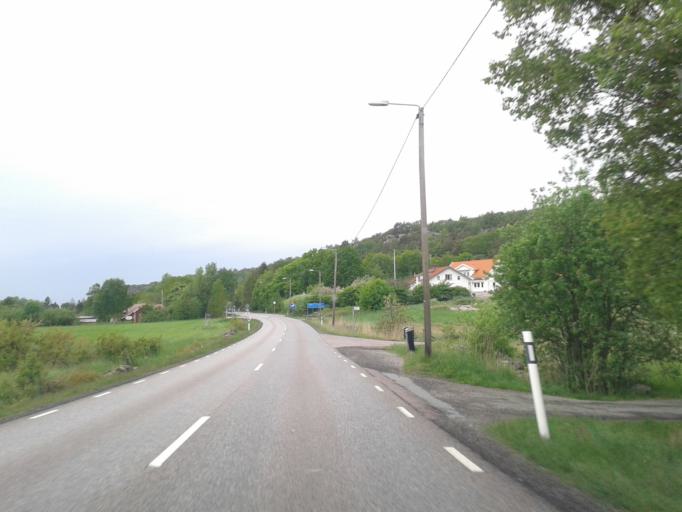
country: SE
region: Vaestra Goetaland
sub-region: Kungalvs Kommun
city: Kode
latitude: 57.8971
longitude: 11.7332
